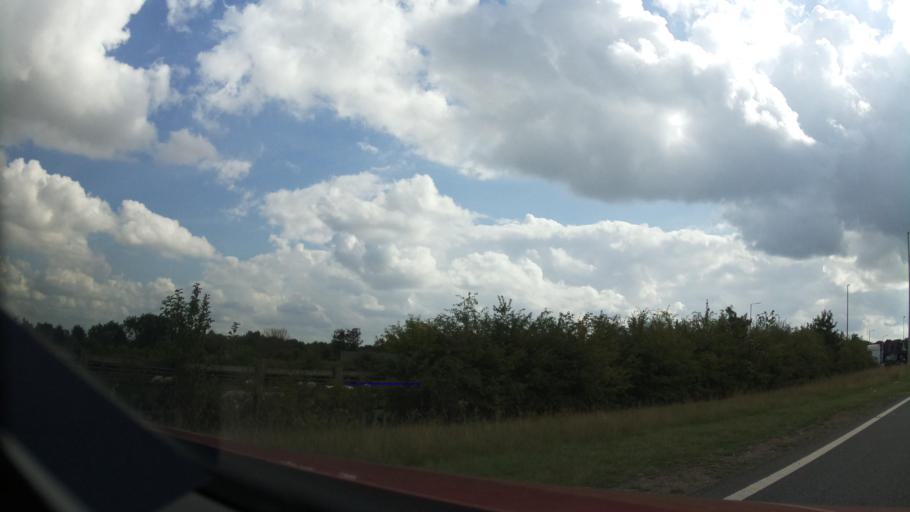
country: GB
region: England
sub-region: North Yorkshire
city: Catterick
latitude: 54.4471
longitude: -1.6701
